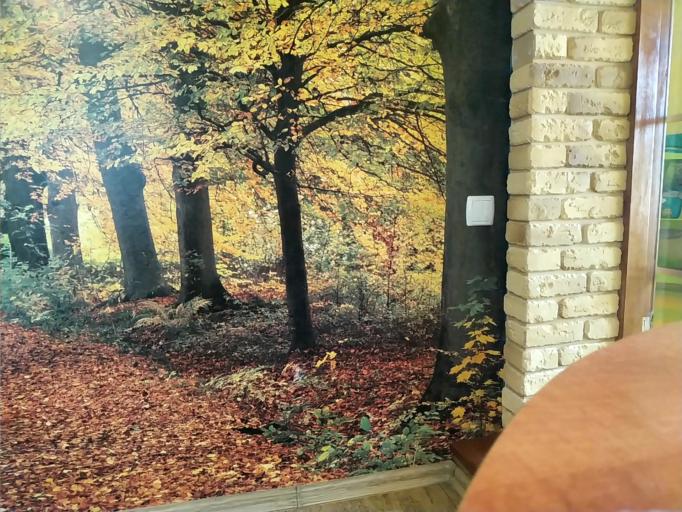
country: RU
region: Arkhangelskaya
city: Onega
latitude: 63.7217
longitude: 38.0843
